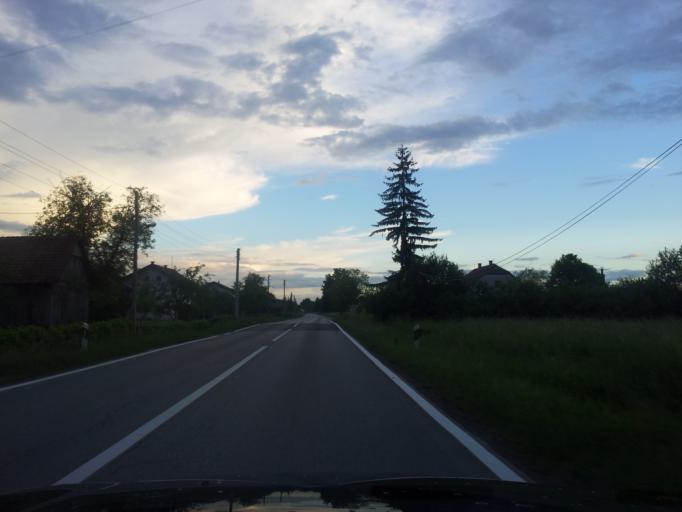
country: HR
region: Karlovacka
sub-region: Grad Karlovac
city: Karlovac
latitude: 45.5598
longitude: 15.5789
